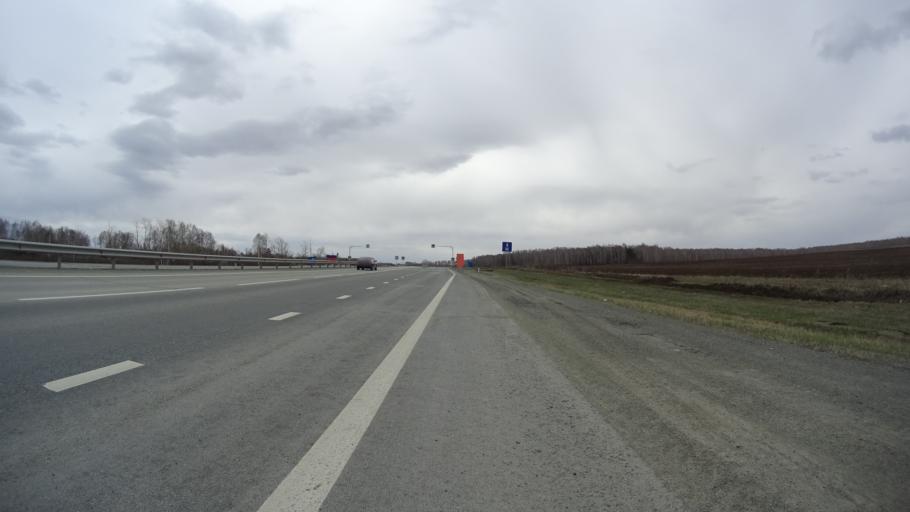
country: RU
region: Chelyabinsk
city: Yemanzhelinka
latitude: 54.8249
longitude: 61.3098
